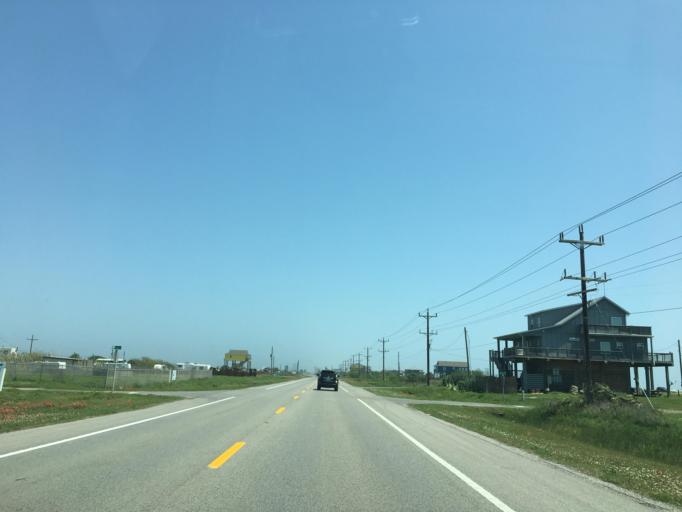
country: US
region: Texas
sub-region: Galveston County
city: Bolivar Peninsula
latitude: 29.5002
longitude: -94.5218
